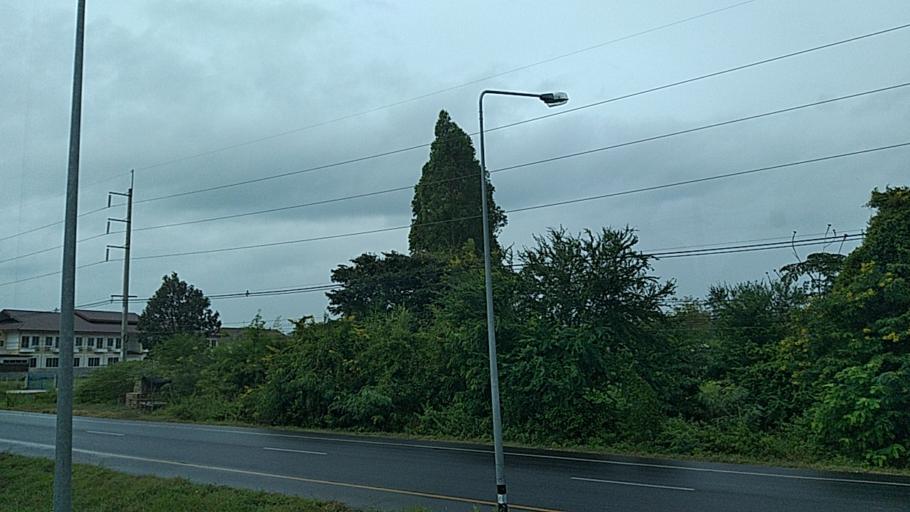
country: TH
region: Maha Sarakham
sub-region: Amphoe Borabue
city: Borabue
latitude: 16.0712
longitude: 103.1496
